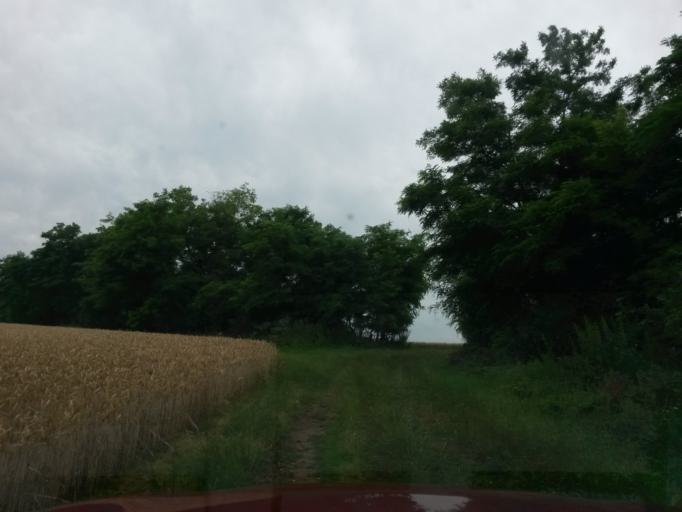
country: SK
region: Nitriansky
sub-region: Okres Nitra
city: Nitra
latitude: 48.3520
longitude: 17.9827
